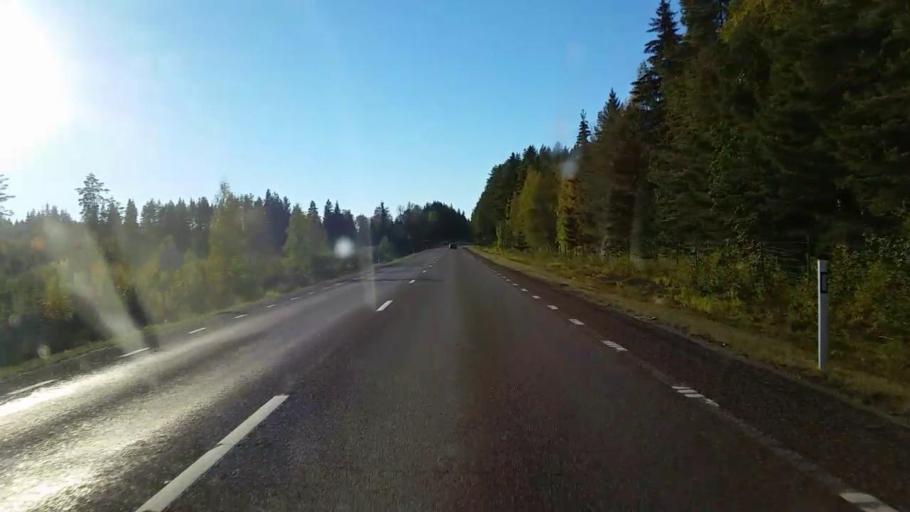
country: SE
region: Gaevleborg
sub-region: Ljusdals Kommun
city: Jaervsoe
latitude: 61.8060
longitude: 16.2489
